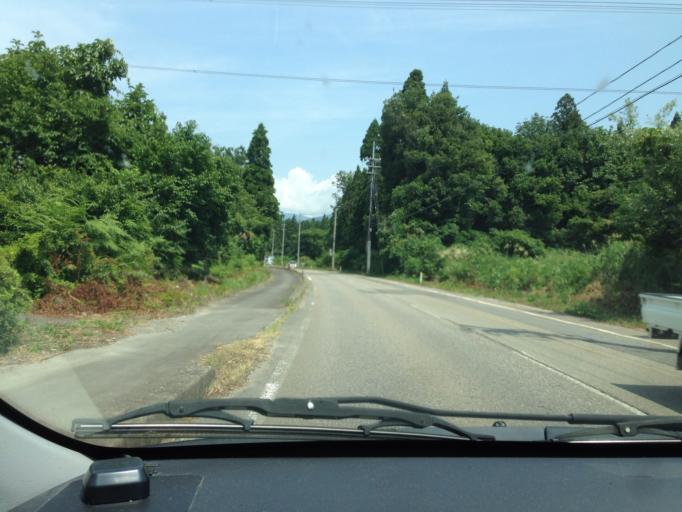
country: JP
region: Fukushima
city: Kitakata
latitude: 37.7067
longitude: 139.8780
